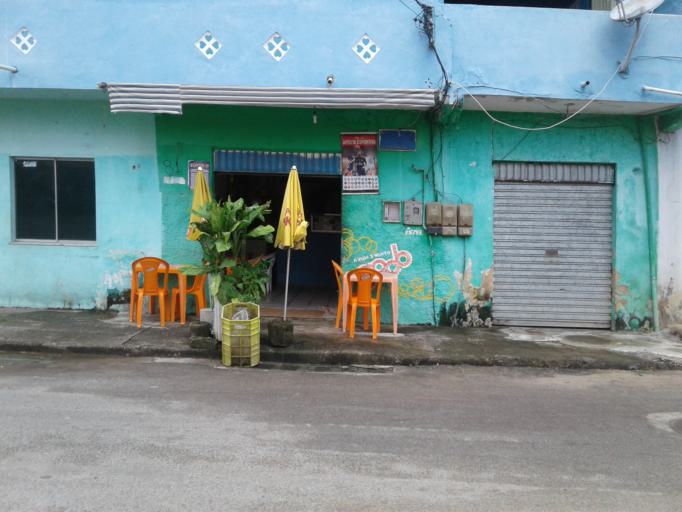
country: BR
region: Bahia
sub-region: Salvador
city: Salvador
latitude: -12.8829
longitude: -38.4738
